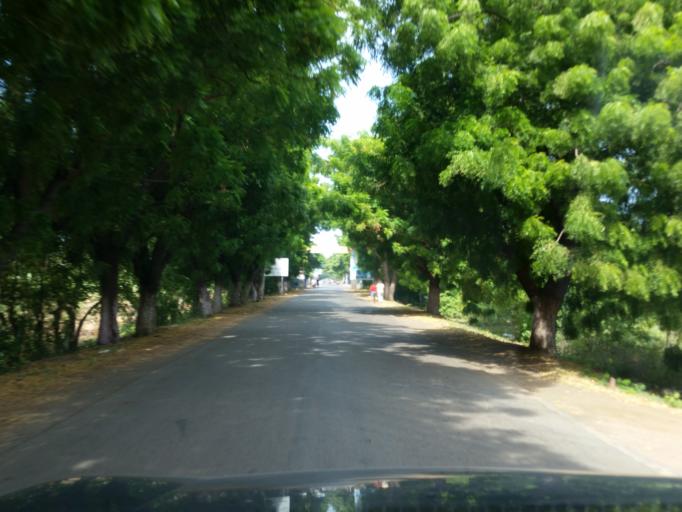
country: NI
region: Managua
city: Masachapa
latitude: 11.7872
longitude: -86.5103
